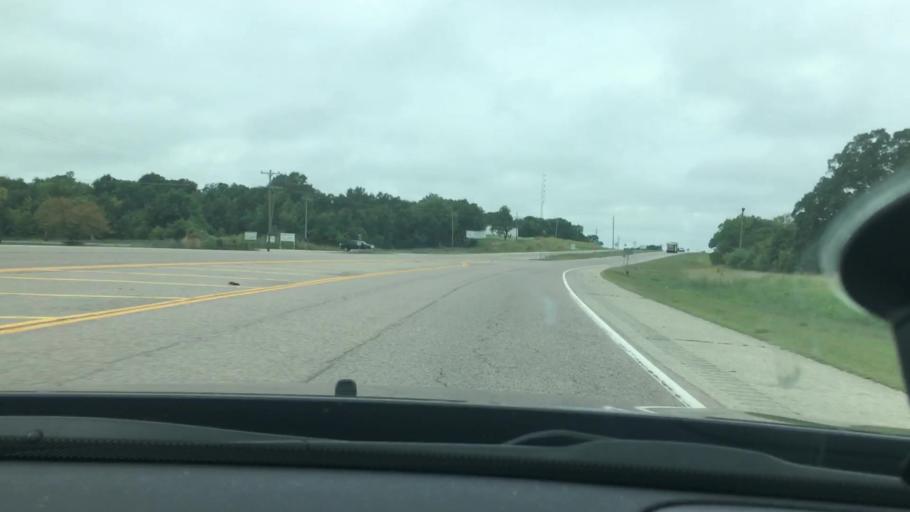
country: US
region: Oklahoma
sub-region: Pontotoc County
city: Ada
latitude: 34.7789
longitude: -96.5846
